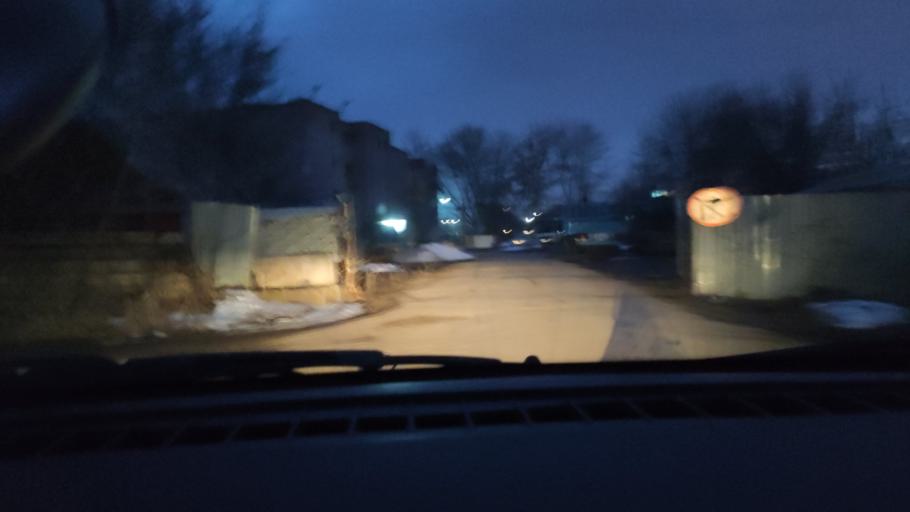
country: RU
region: Samara
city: Samara
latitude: 53.2129
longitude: 50.2657
